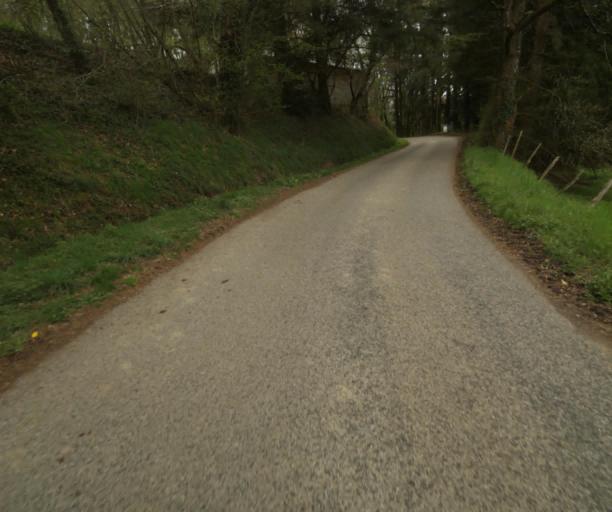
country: FR
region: Limousin
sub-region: Departement de la Correze
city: Laguenne
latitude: 45.2486
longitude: 1.8545
